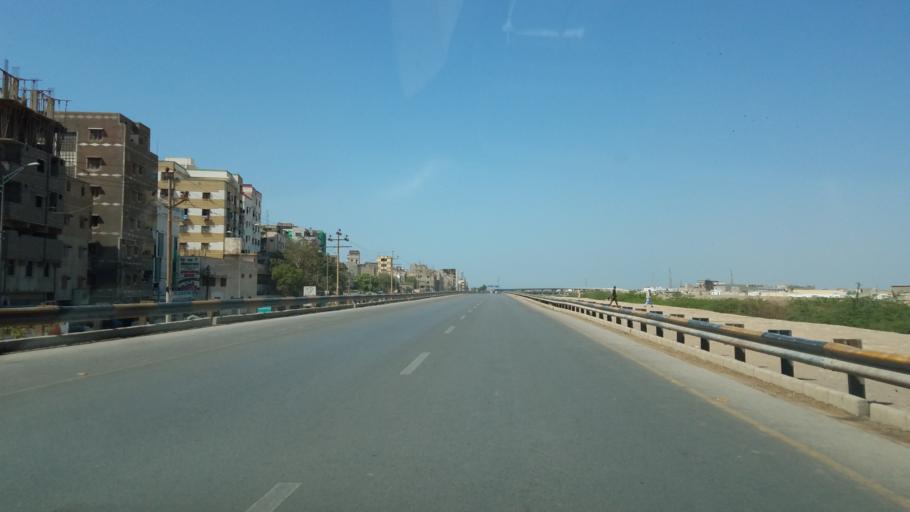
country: PK
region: Sindh
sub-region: Karachi District
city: Karachi
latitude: 24.8759
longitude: 66.9864
